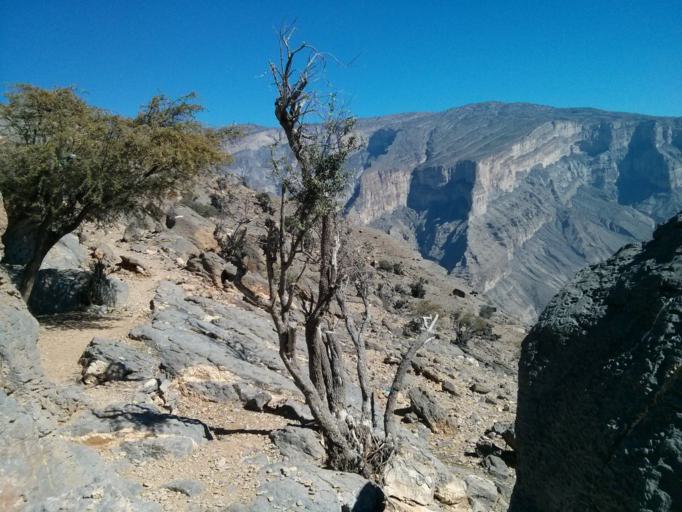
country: OM
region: Muhafazat ad Dakhiliyah
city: Bahla'
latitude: 23.1934
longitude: 57.2021
